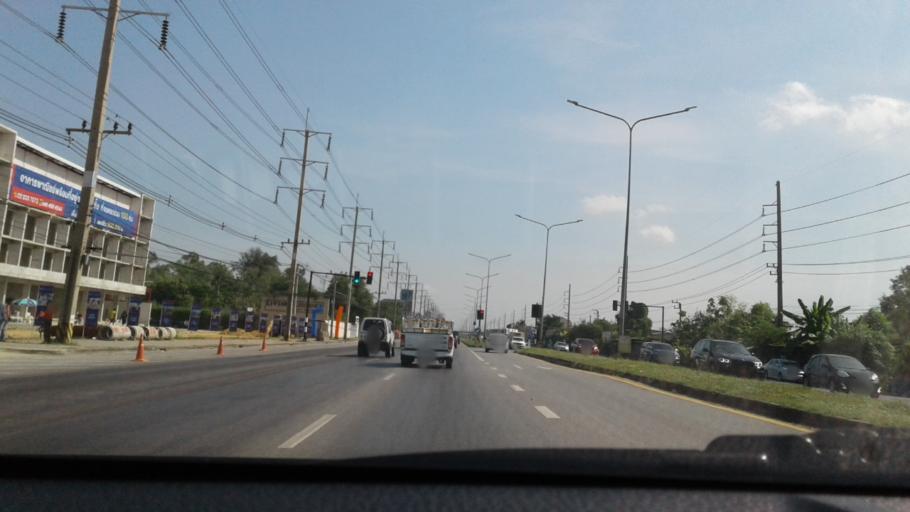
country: TH
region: Phra Nakhon Si Ayutthaya
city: Ban Bang Kadi Pathum Thani
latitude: 13.9739
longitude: 100.5735
